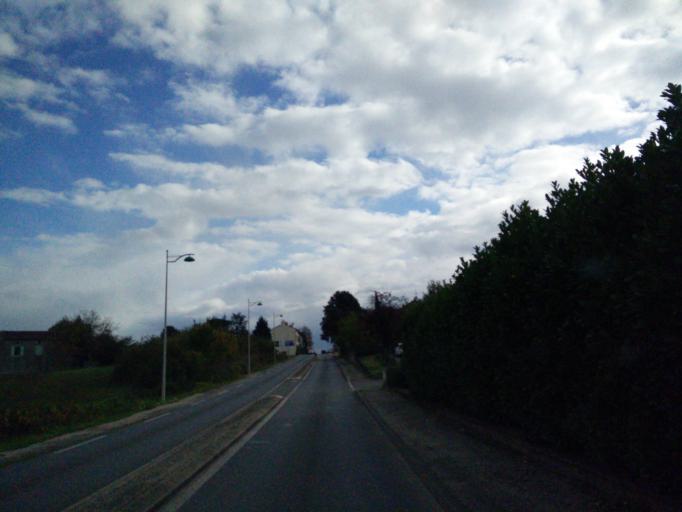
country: FR
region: Midi-Pyrenees
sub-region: Departement du Lot
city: Pradines
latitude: 44.4996
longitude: 1.3841
